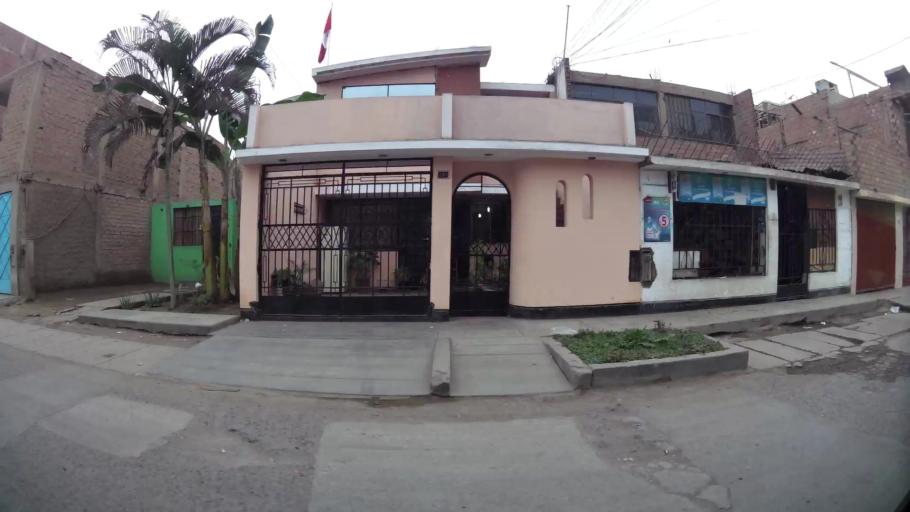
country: PE
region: Lima
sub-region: Lima
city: Independencia
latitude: -11.9503
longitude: -77.0903
